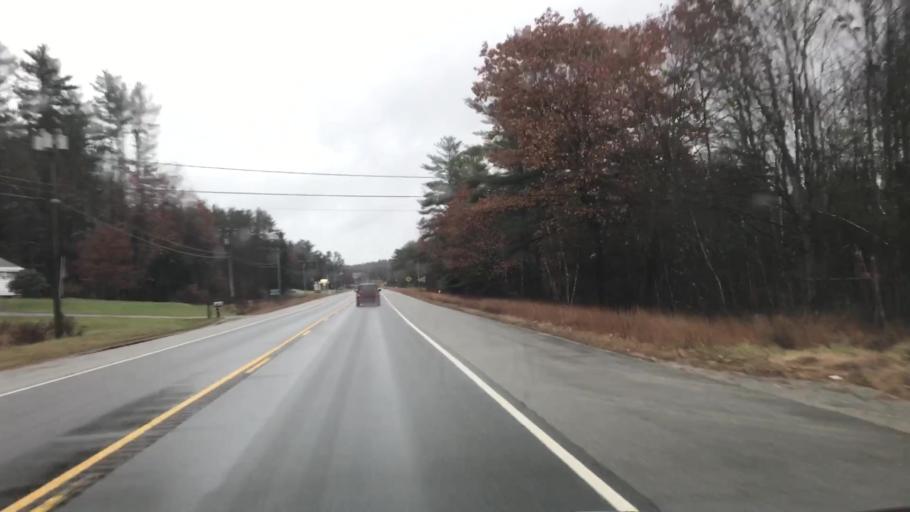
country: US
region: New Hampshire
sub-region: Belknap County
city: Barnstead
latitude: 43.3268
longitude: -71.3043
